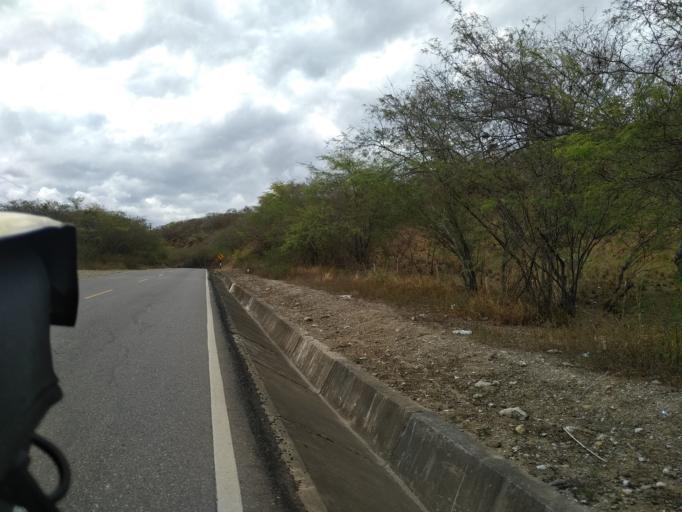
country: PE
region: Amazonas
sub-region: Utcubamba
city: Jamalca
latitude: -5.8254
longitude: -78.2566
